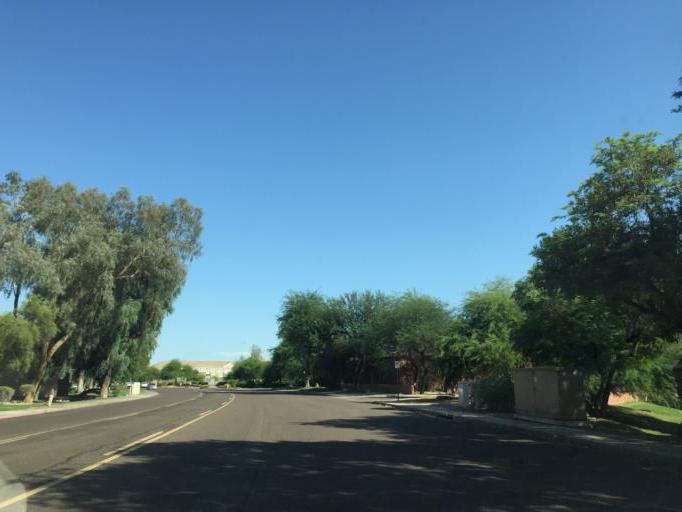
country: US
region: Arizona
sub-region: Maricopa County
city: Paradise Valley
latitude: 33.5976
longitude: -111.9867
